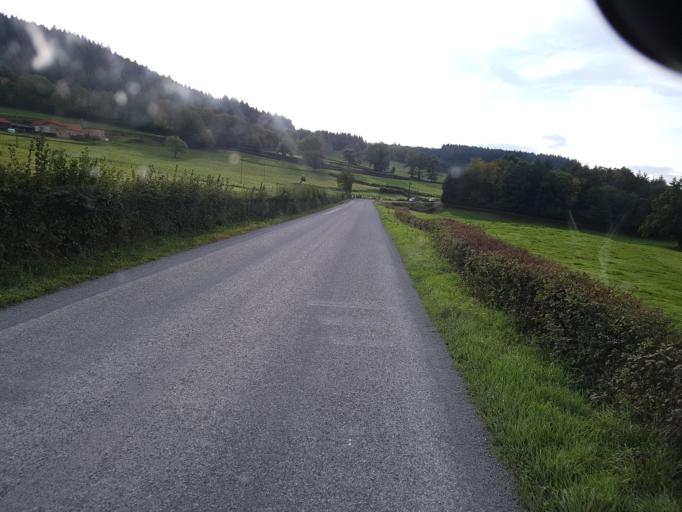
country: FR
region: Bourgogne
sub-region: Departement de Saone-et-Loire
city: Chauffailles
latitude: 46.2605
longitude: 4.4010
